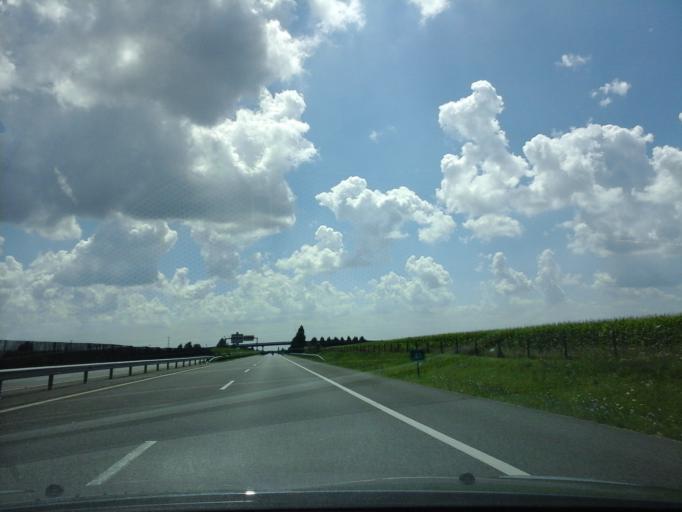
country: HU
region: Hajdu-Bihar
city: Ebes
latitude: 47.5235
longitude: 21.5503
